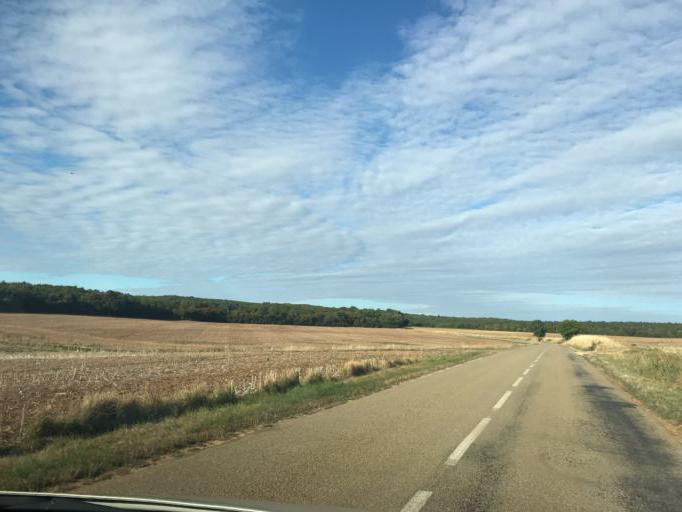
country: FR
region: Bourgogne
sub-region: Departement de l'Yonne
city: Fontenailles
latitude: 47.5599
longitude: 3.4362
